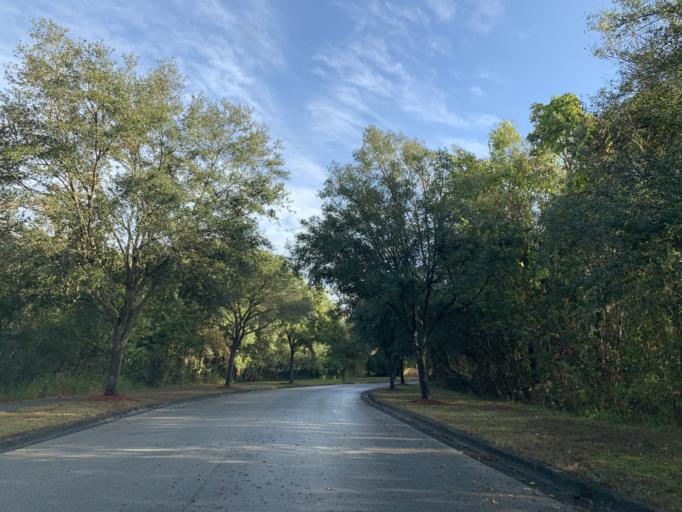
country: US
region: Florida
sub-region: Hillsborough County
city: Mango
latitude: 27.9792
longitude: -82.3219
